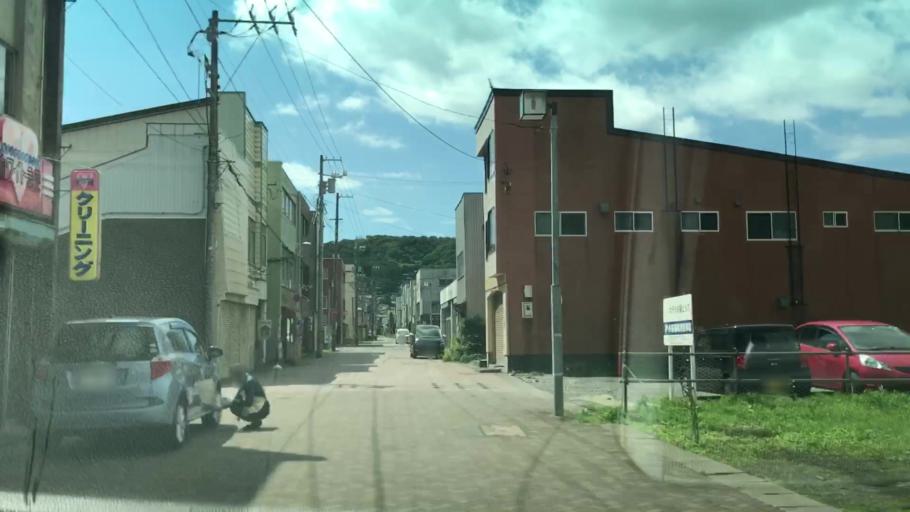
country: JP
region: Hokkaido
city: Muroran
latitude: 42.3351
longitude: 141.0119
